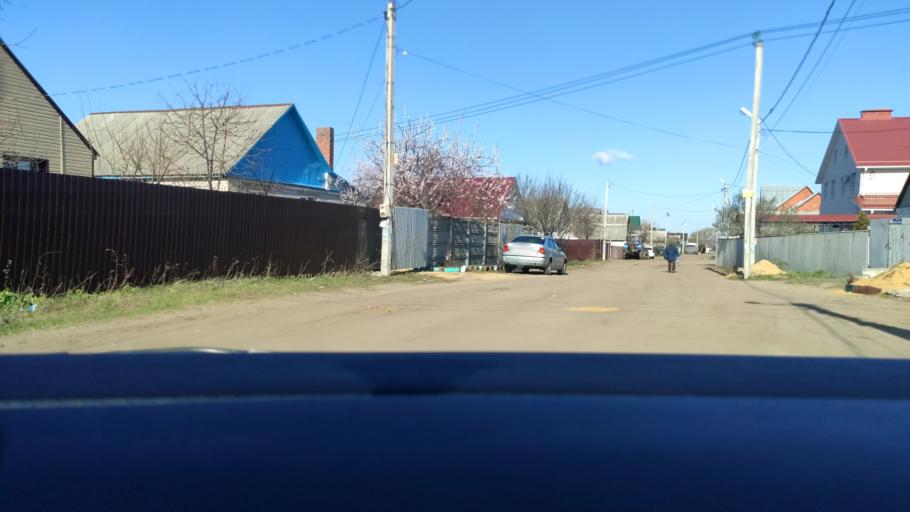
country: RU
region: Voronezj
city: Podgornoye
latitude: 51.7257
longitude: 39.1550
